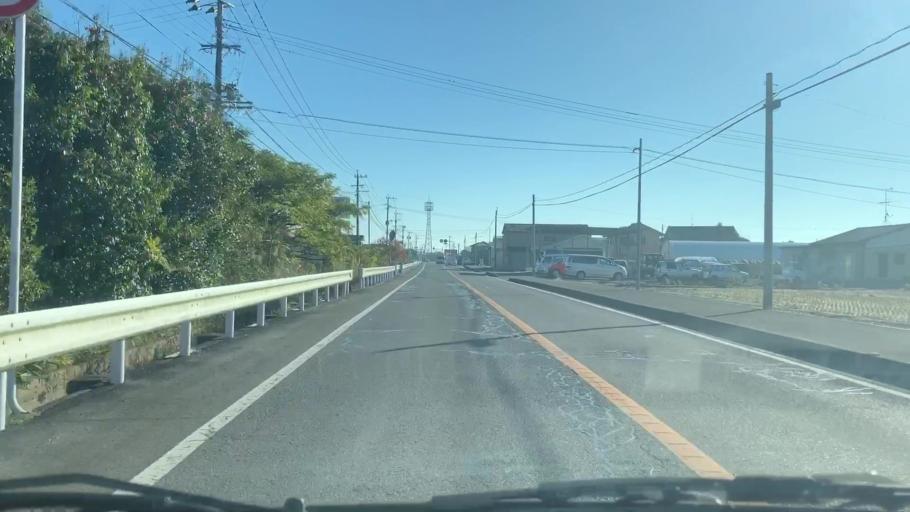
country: JP
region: Saga Prefecture
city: Kashima
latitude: 33.1830
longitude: 130.1764
